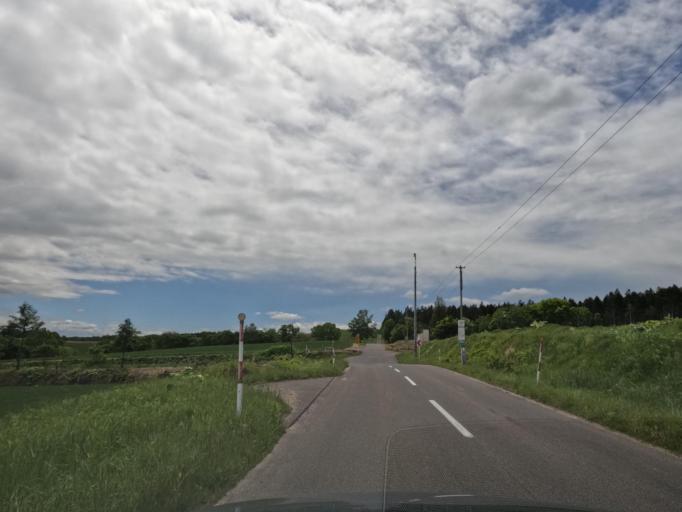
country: JP
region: Hokkaido
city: Shimo-furano
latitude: 43.5007
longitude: 142.4130
